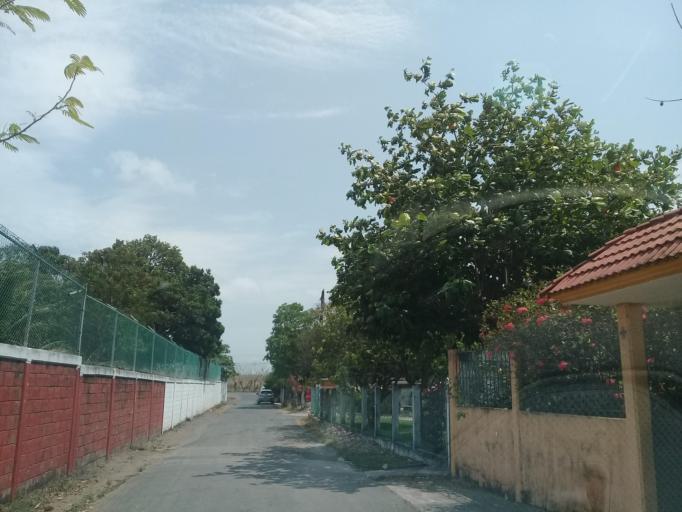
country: MX
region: Veracruz
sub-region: Veracruz
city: Delfino Victoria (Santa Fe)
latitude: 19.1746
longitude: -96.2745
